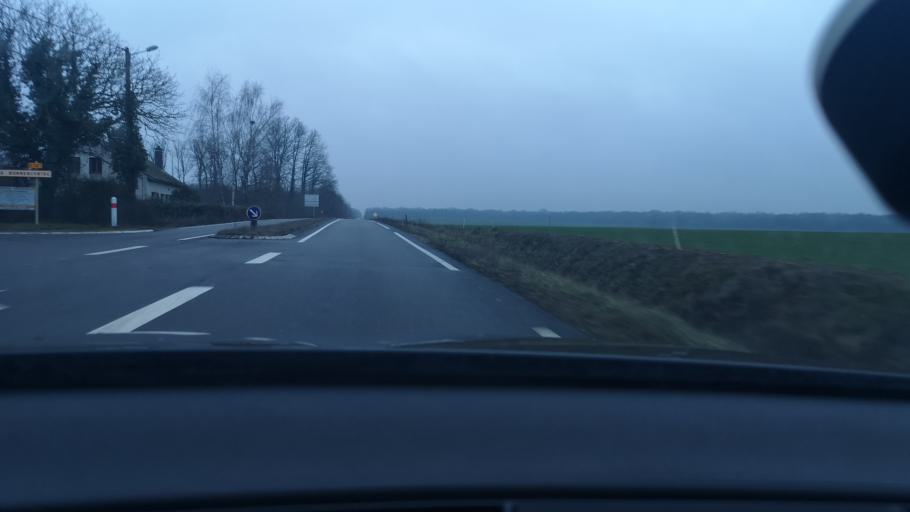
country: FR
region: Bourgogne
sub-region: Departement de la Cote-d'Or
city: Aiserey
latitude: 47.1217
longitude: 5.0993
